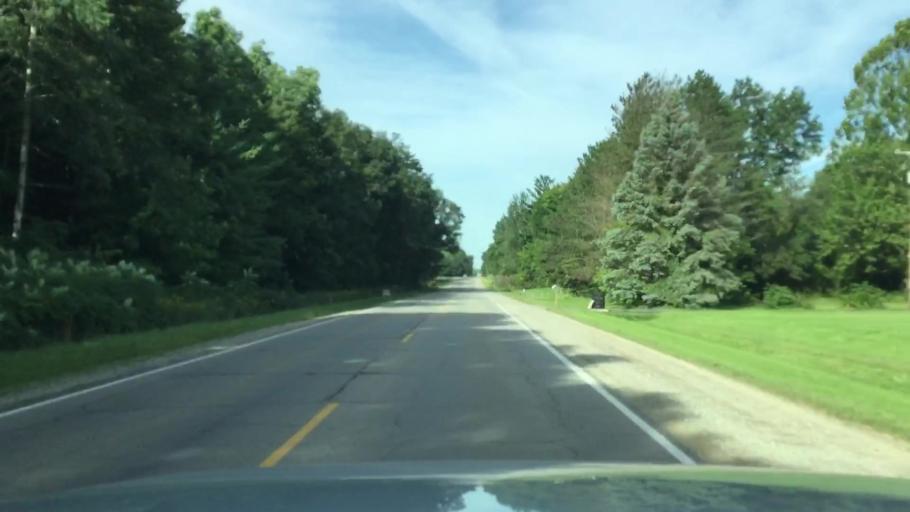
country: US
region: Michigan
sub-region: Genesee County
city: Flushing
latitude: 43.1179
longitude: -83.8349
